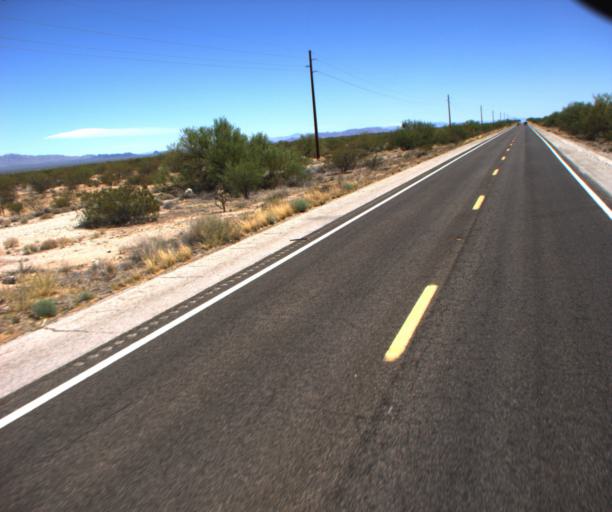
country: US
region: Arizona
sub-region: La Paz County
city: Salome
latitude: 33.8651
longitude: -113.4081
